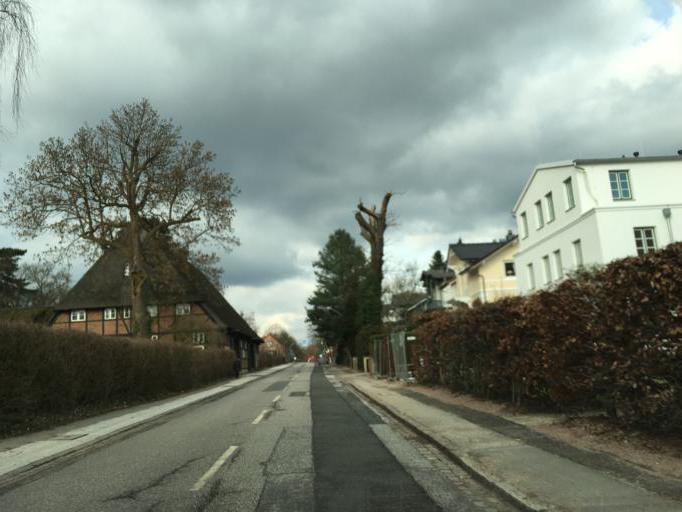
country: DE
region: Hamburg
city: Eidelstedt
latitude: 53.5554
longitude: 9.8652
